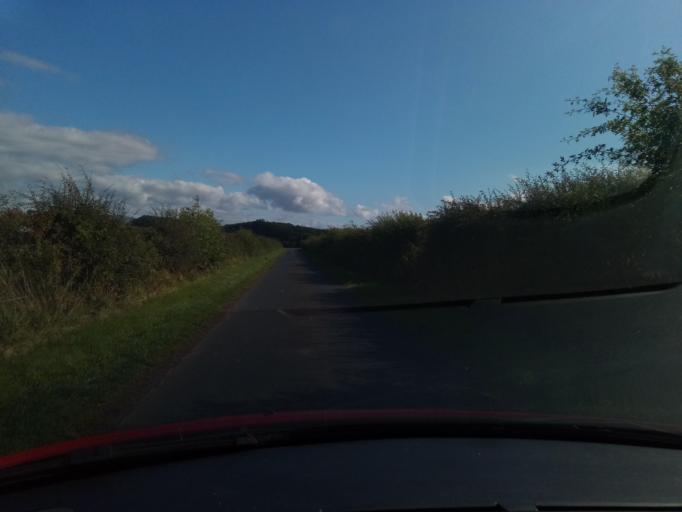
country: GB
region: Scotland
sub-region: The Scottish Borders
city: Jedburgh
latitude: 55.5093
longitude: -2.4778
